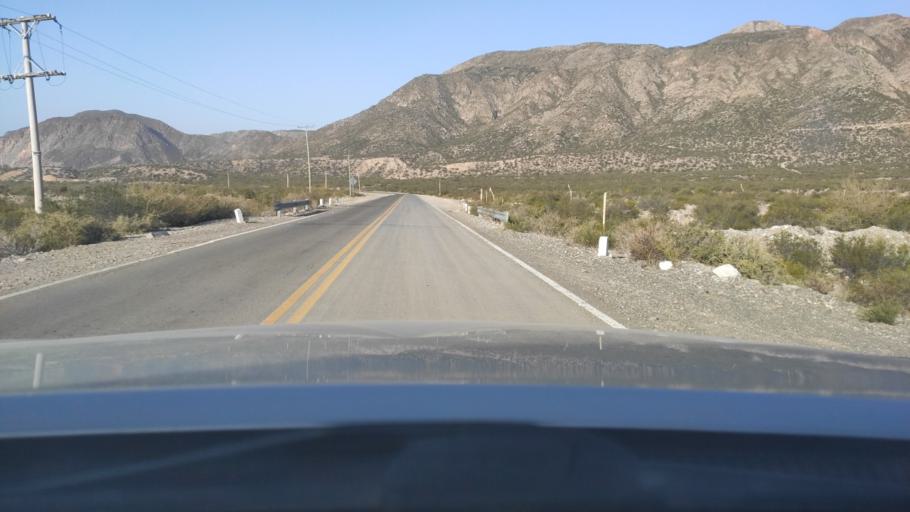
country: AR
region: San Juan
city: Villa Media Agua
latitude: -32.0085
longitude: -68.7741
